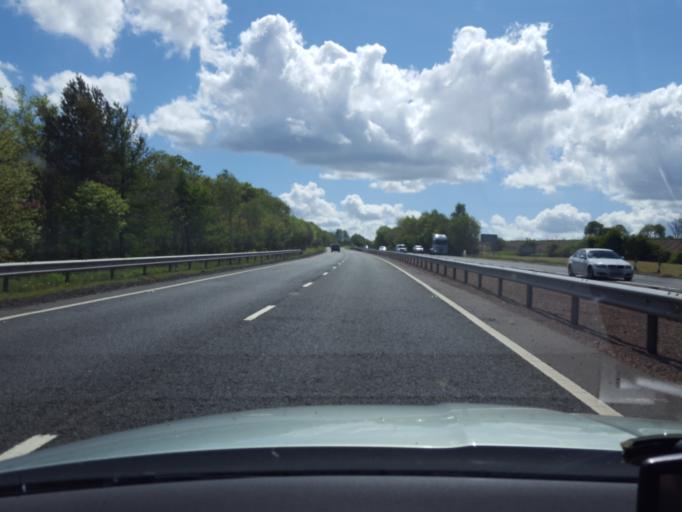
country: GB
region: Scotland
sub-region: Angus
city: Forfar
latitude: 56.5856
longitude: -2.9131
